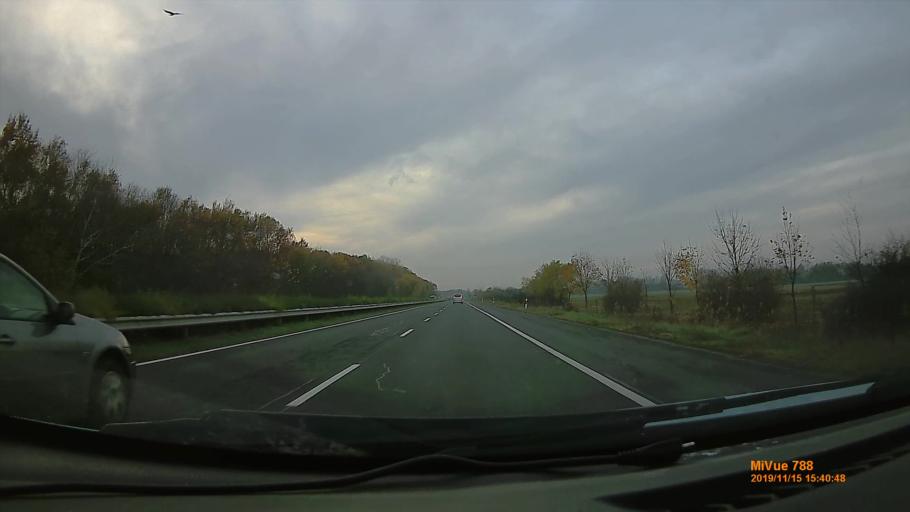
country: HU
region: Bekes
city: Bekescsaba
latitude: 46.6750
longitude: 21.1449
